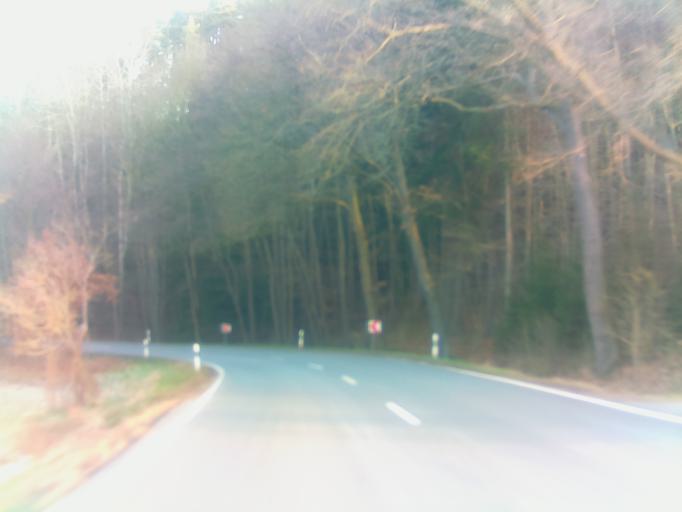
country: DE
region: Thuringia
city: Freienorla
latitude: 50.7536
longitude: 11.5543
